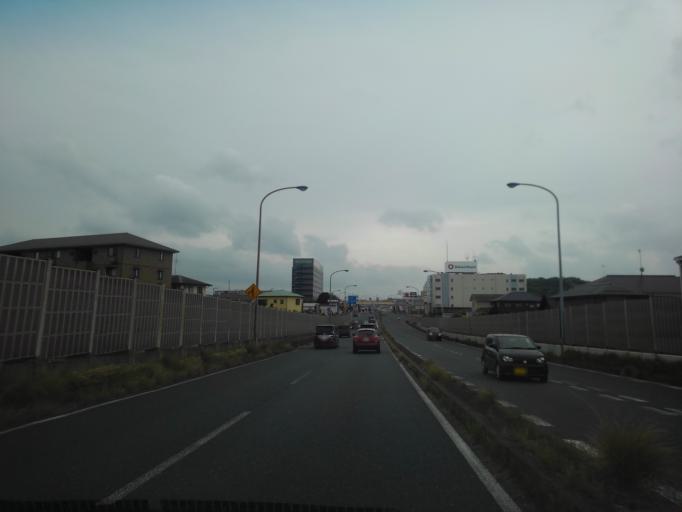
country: JP
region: Chiba
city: Kisarazu
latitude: 35.3846
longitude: 139.9418
